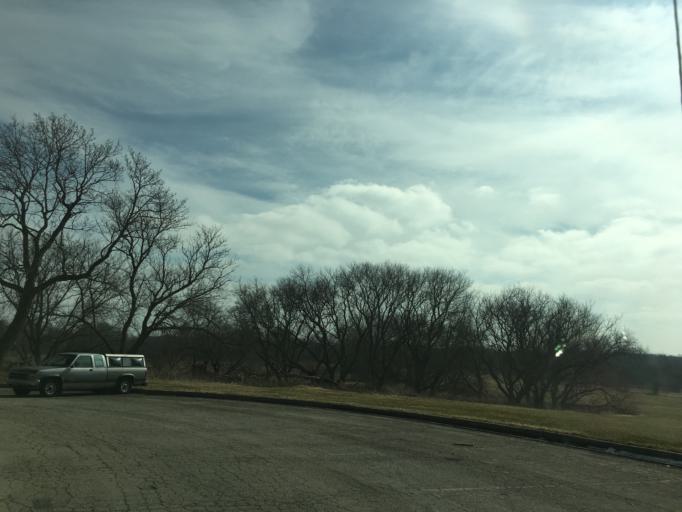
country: US
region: Illinois
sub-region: Cook County
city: Streamwood
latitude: 42.0485
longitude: -88.1975
